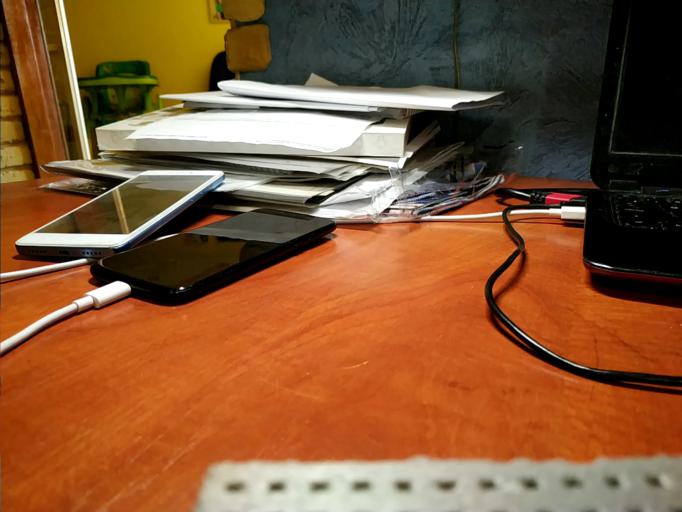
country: RU
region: Tverskaya
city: Kalashnikovo
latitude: 57.4089
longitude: 35.1792
